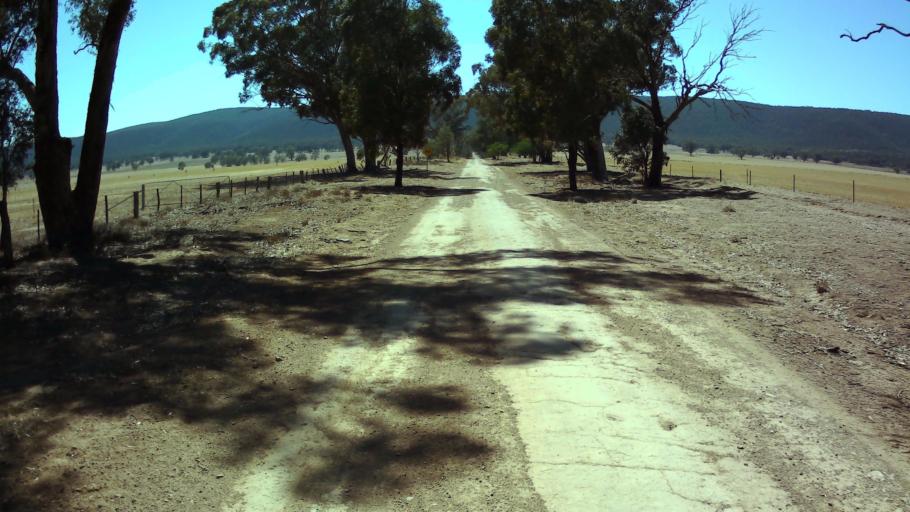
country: AU
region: New South Wales
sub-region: Weddin
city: Grenfell
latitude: -33.7022
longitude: 148.3249
